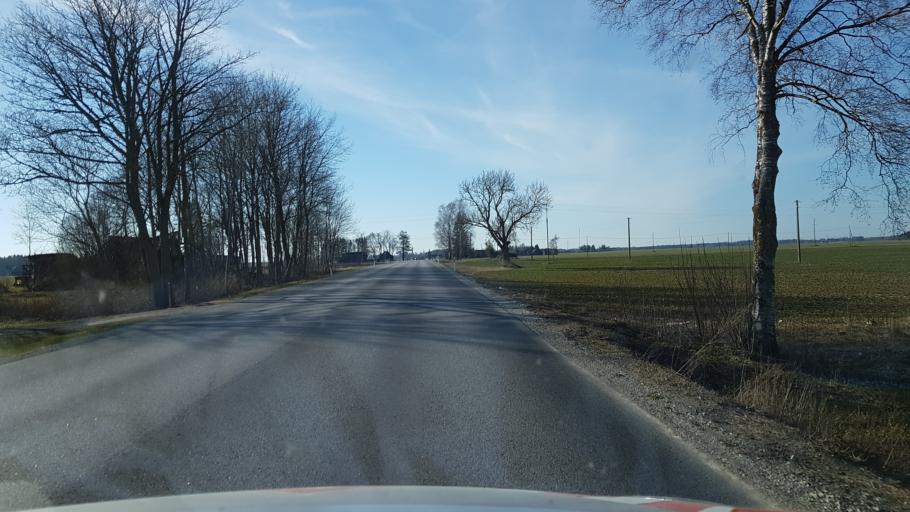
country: EE
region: Laeaene-Virumaa
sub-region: Vinni vald
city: Vinni
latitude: 59.2334
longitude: 26.5052
